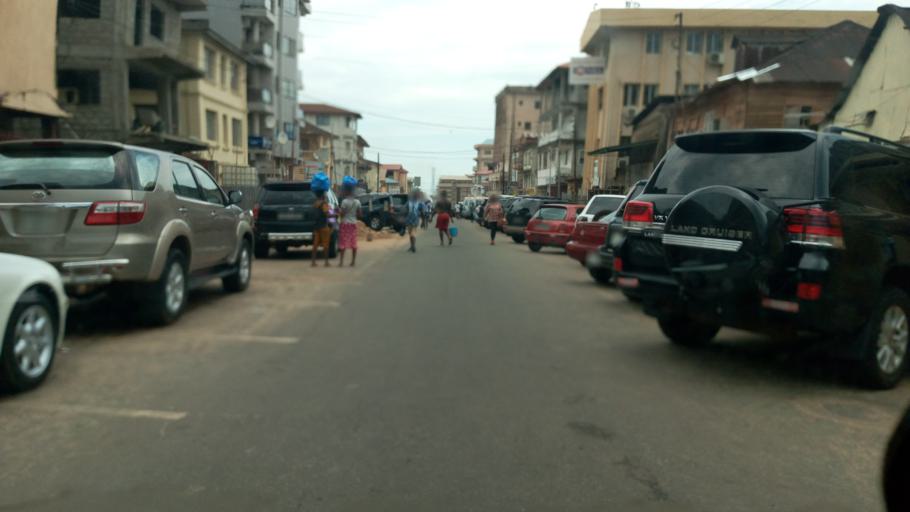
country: SL
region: Western Area
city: Freetown
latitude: 8.4838
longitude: -13.2372
